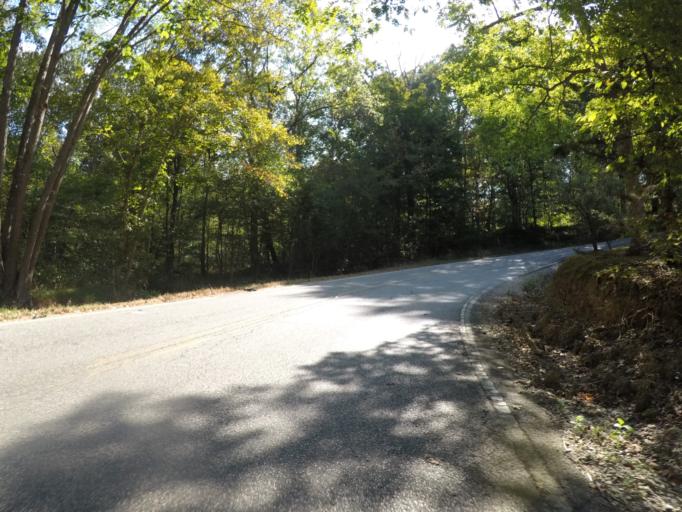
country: US
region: West Virginia
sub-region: Cabell County
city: Lesage
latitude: 38.5922
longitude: -82.4293
